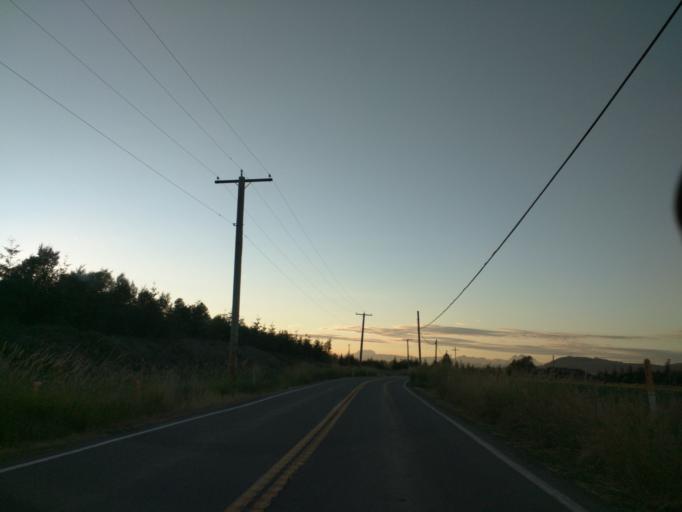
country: US
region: Washington
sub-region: Whatcom County
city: Sumas
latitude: 48.9798
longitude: -122.2368
